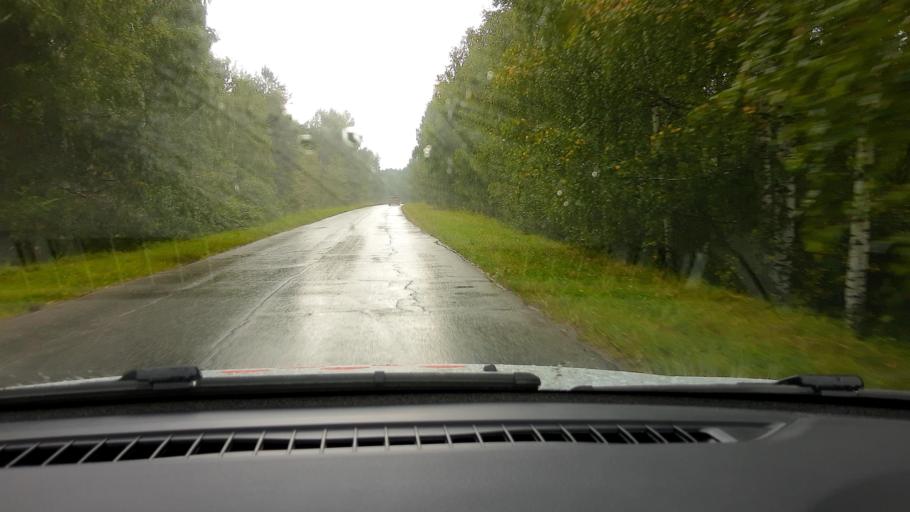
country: RU
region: Nizjnij Novgorod
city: Dal'neye Konstantinovo
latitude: 55.9513
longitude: 43.9615
